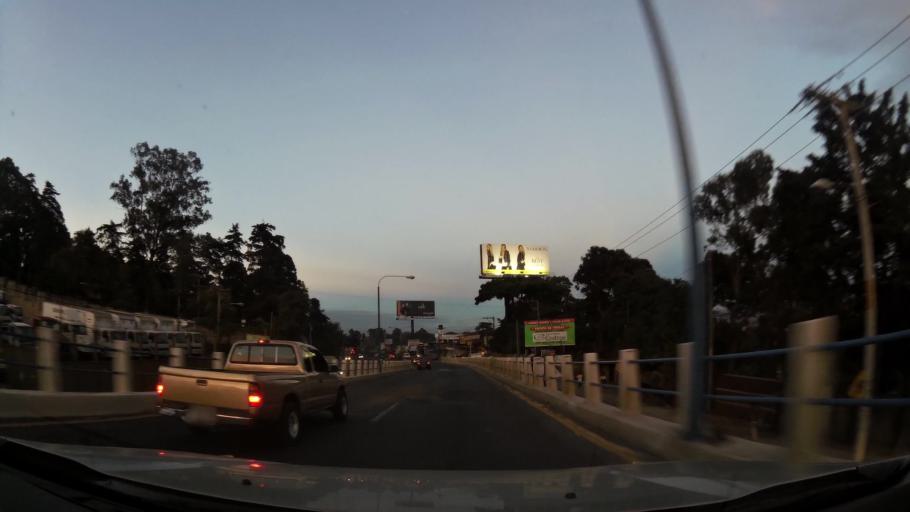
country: GT
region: Guatemala
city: Mixco
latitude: 14.6182
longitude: -90.6059
